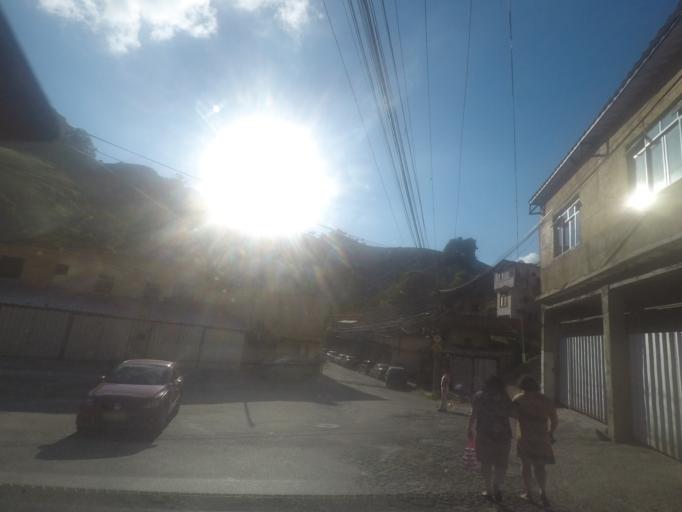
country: BR
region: Rio de Janeiro
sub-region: Petropolis
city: Petropolis
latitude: -22.4977
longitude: -43.1475
